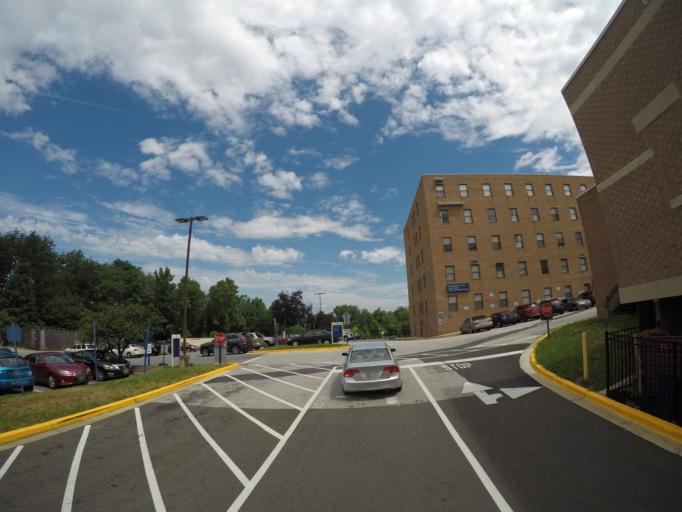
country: US
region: Maryland
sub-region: Prince George's County
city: Goddard
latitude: 38.9829
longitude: -76.8658
